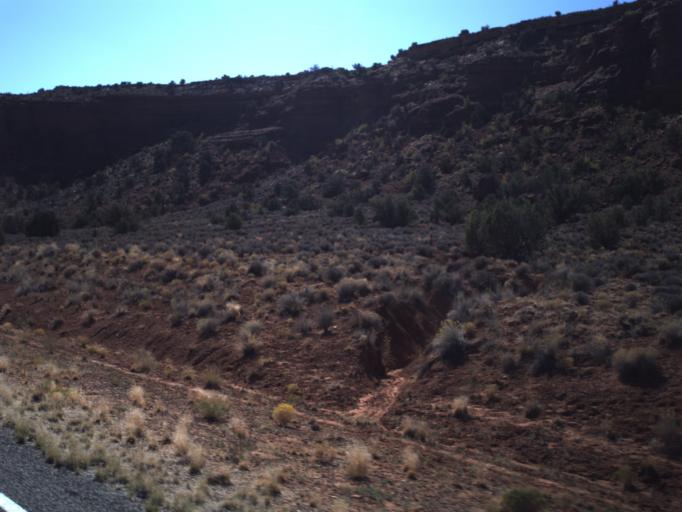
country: US
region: Utah
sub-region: San Juan County
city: Blanding
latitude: 37.6925
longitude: -110.2284
